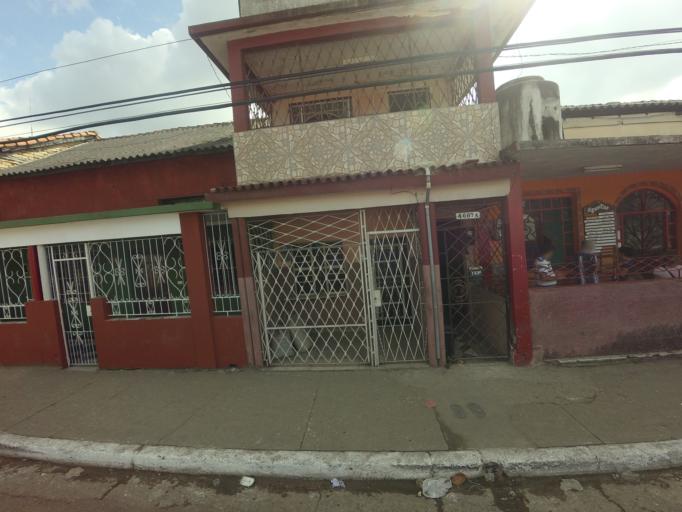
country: CU
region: Artemisa
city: Bauta
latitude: 23.0160
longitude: -82.4984
